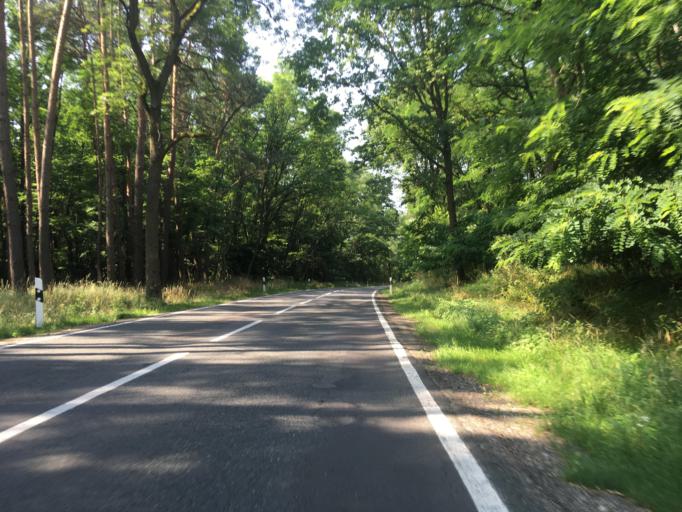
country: DE
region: Brandenburg
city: Golzow
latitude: 52.2892
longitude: 12.6652
